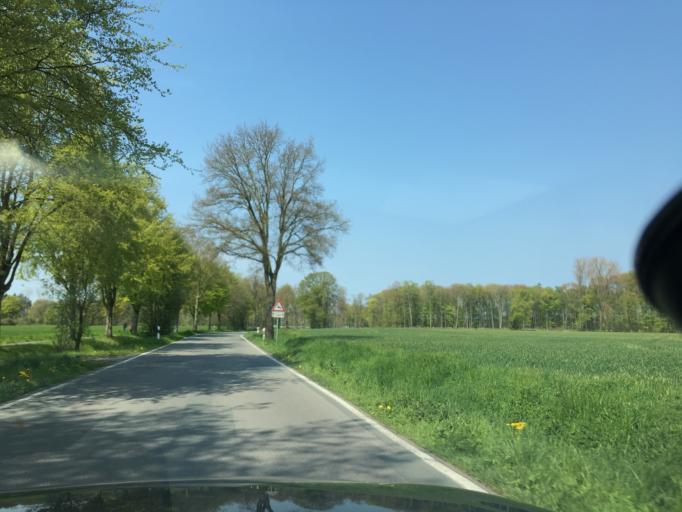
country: DE
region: North Rhine-Westphalia
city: Ludinghausen
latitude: 51.7782
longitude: 7.4388
